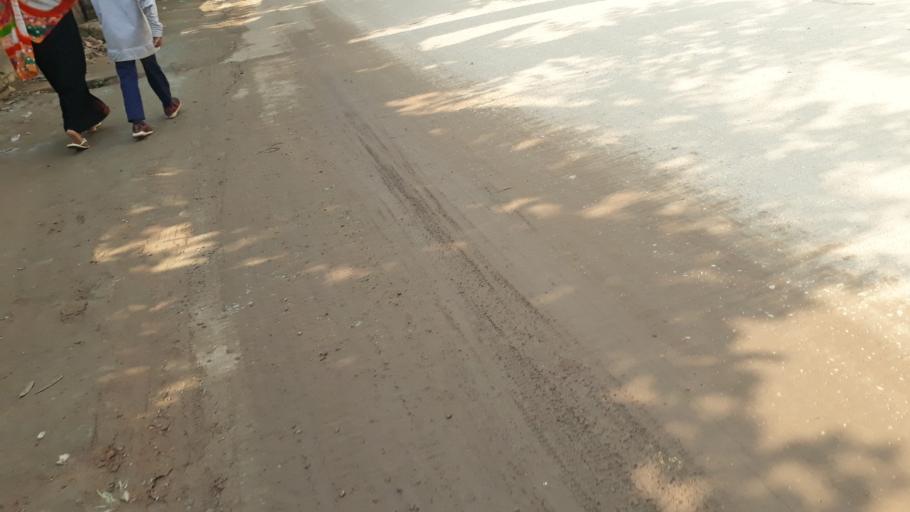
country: BD
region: Dhaka
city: Tungi
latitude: 23.8578
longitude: 90.2606
